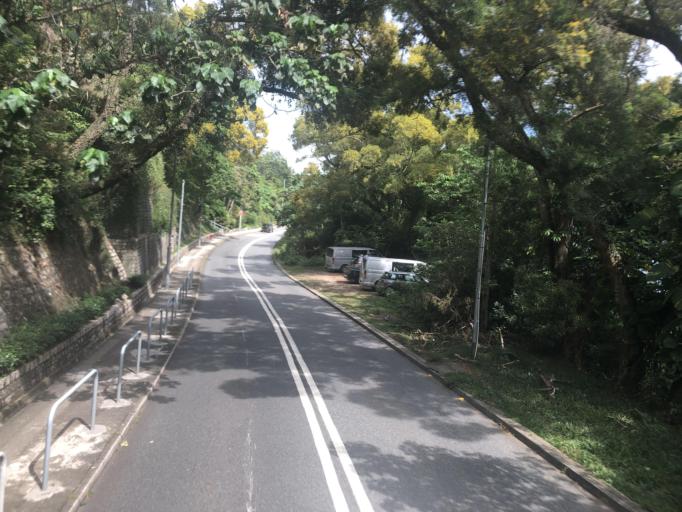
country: HK
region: Sai Kung
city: Sai Kung
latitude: 22.3895
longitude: 114.2915
